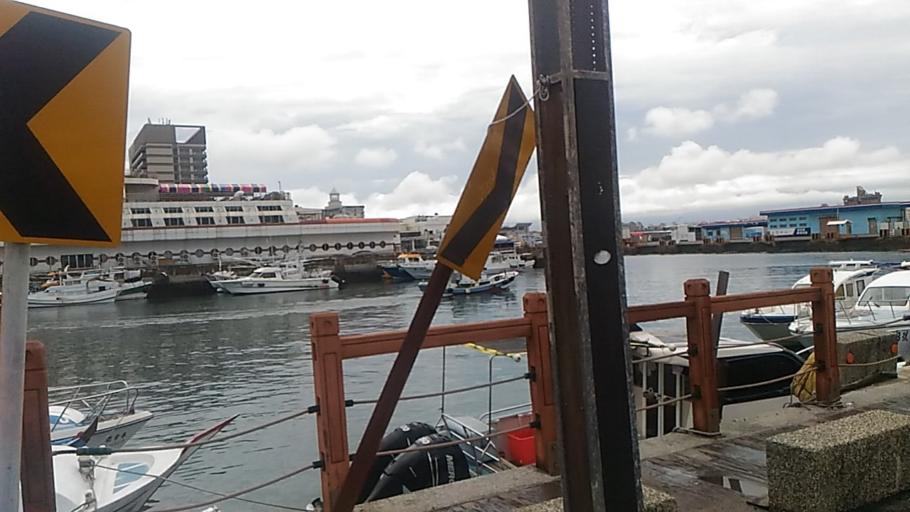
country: TW
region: Taiwan
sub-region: Penghu
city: Ma-kung
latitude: 23.5649
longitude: 119.5691
